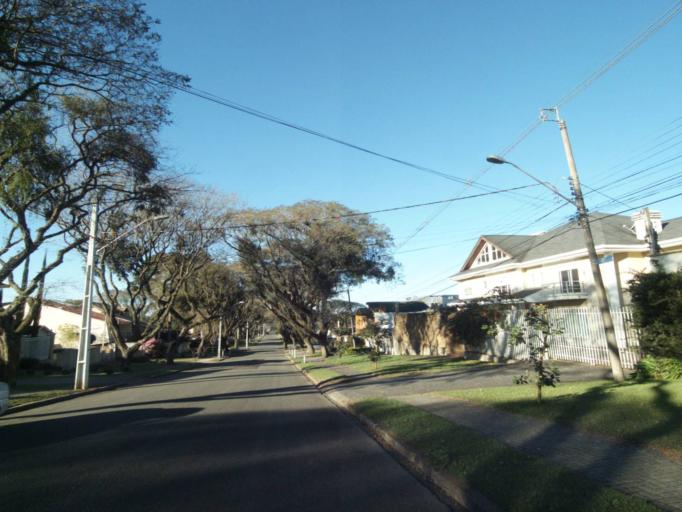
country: BR
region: Parana
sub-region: Curitiba
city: Curitiba
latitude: -25.4225
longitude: -49.2320
